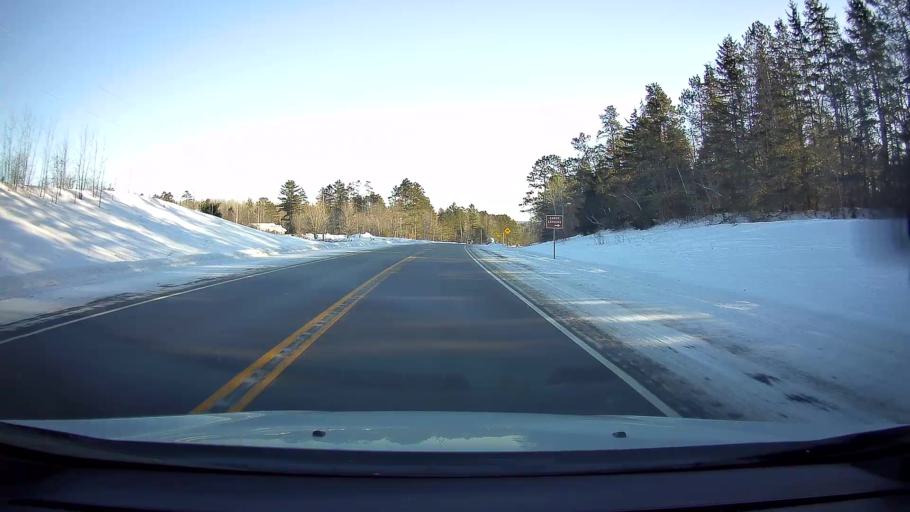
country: US
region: Wisconsin
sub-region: Sawyer County
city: Hayward
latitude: 46.0730
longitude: -91.4235
